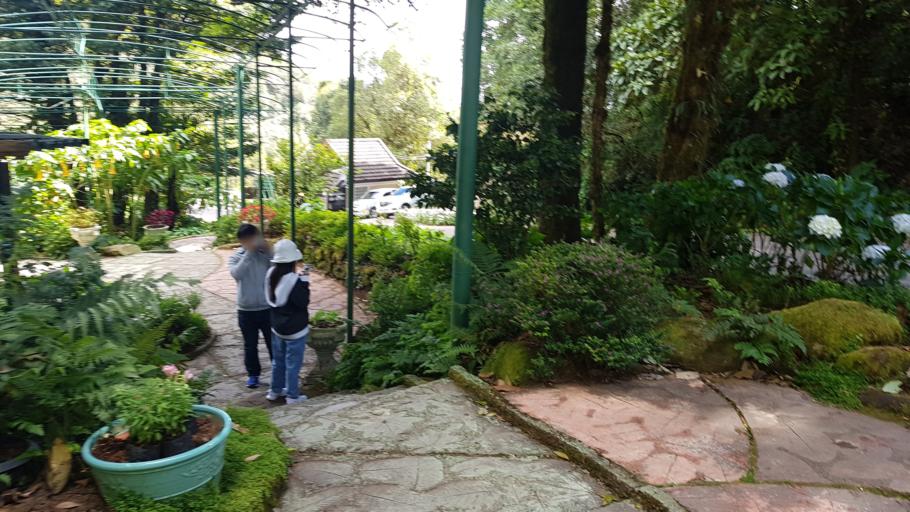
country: TH
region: Chiang Mai
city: Mae Chaem
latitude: 18.5523
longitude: 98.4808
